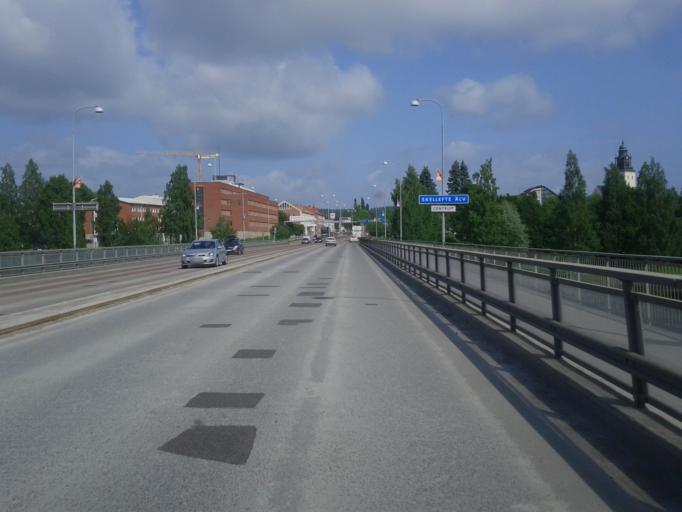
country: SE
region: Vaesterbotten
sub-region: Skelleftea Kommun
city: Skelleftea
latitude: 64.7468
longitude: 20.9599
